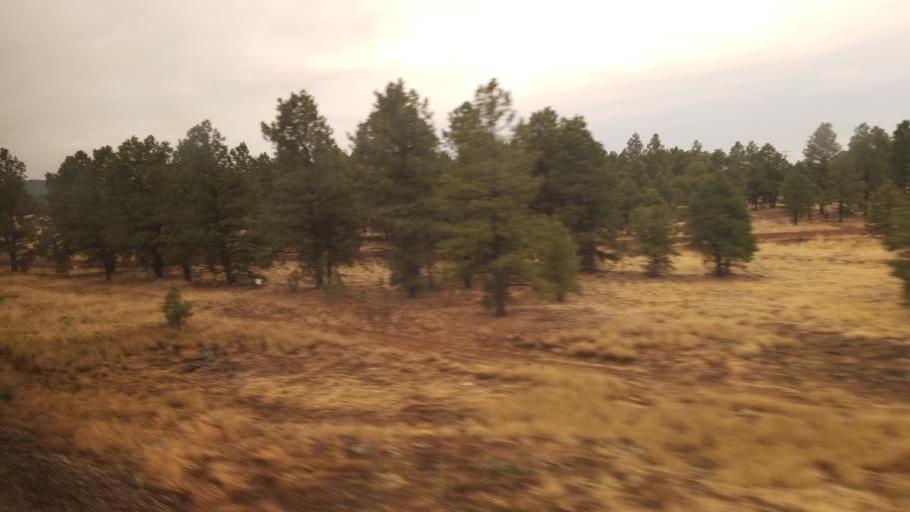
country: US
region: Arizona
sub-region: Coconino County
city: Parks
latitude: 35.2275
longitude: -111.8095
